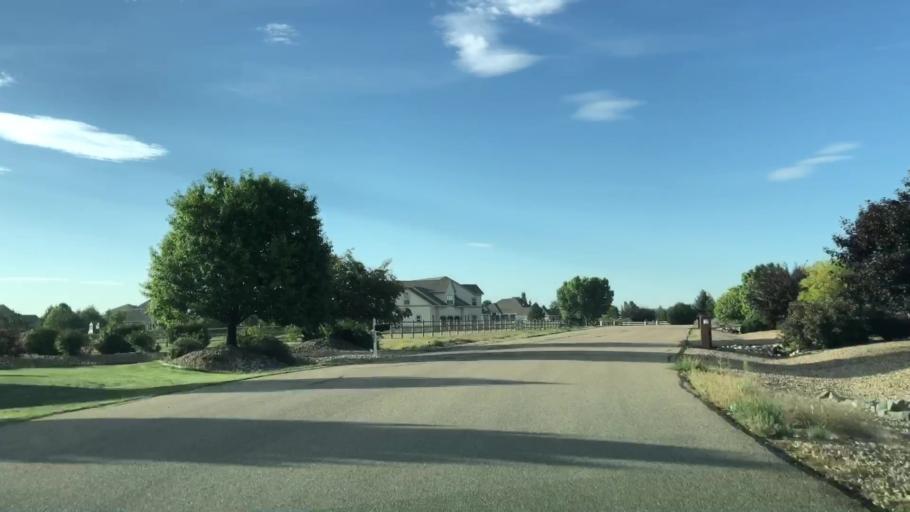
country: US
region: Colorado
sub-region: Weld County
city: Windsor
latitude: 40.4433
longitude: -104.9494
